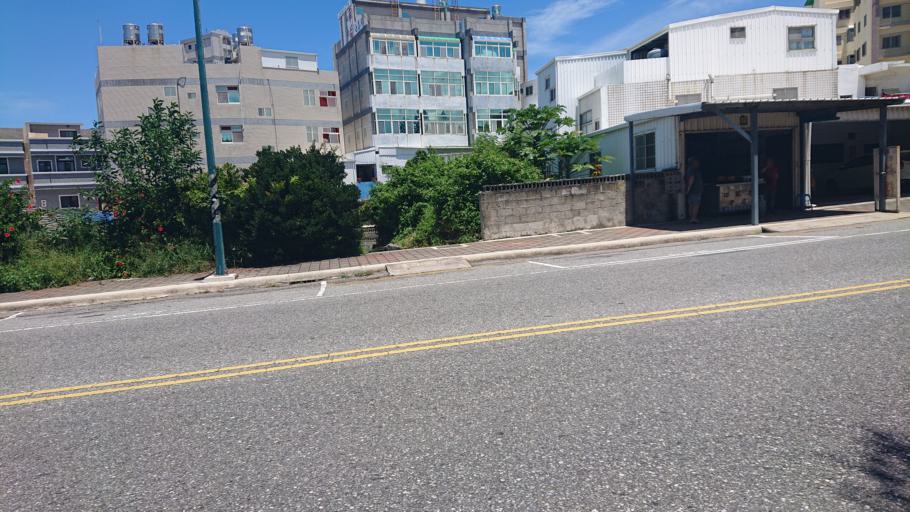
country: TW
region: Taiwan
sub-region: Penghu
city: Ma-kung
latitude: 23.5713
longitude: 119.5763
